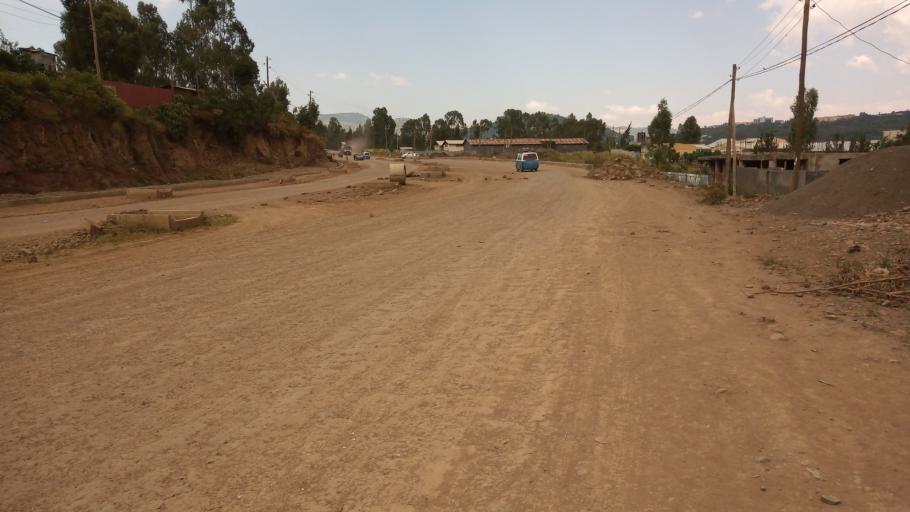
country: ET
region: Amhara
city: Gondar
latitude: 12.5665
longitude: 37.4343
